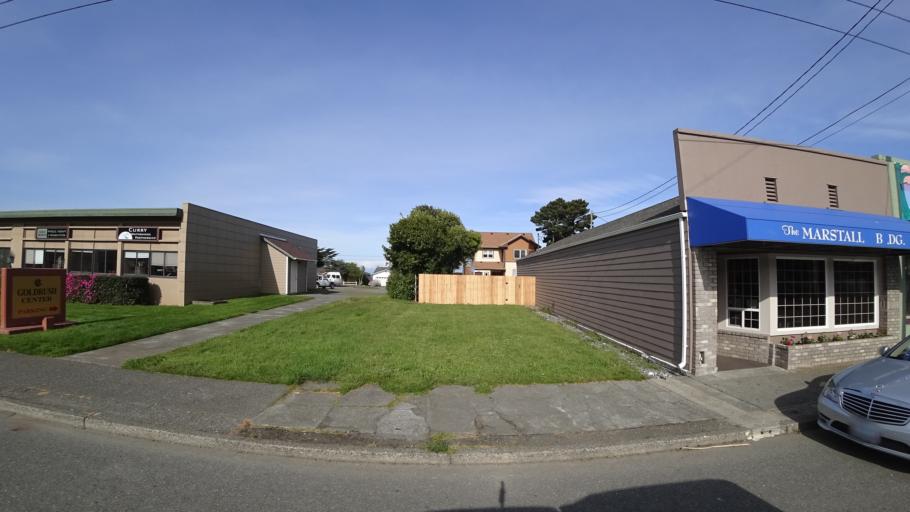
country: US
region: Oregon
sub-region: Curry County
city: Gold Beach
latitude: 42.4142
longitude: -124.4209
